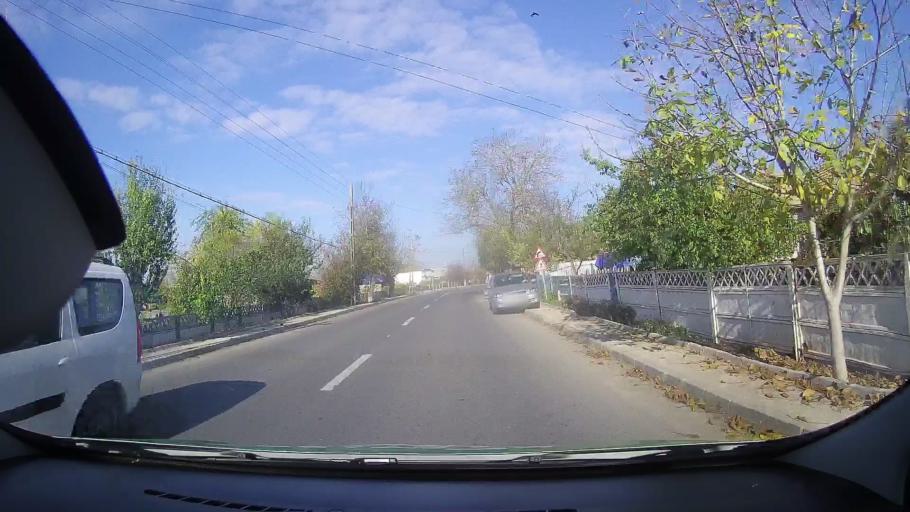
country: RO
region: Tulcea
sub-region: Comuna Valea Nucarilor
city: Valea Nucarilor
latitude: 45.0367
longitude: 28.9407
